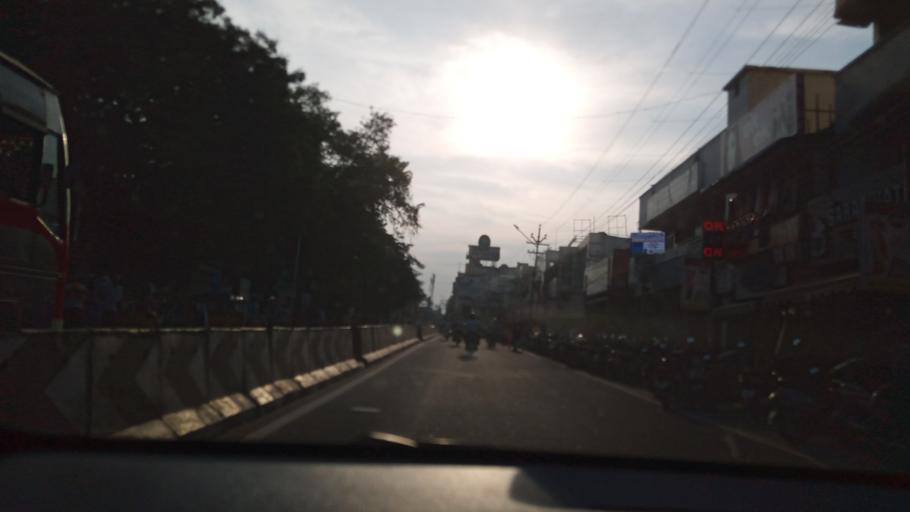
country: IN
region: Tamil Nadu
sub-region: Coimbatore
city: Coimbatore
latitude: 10.9938
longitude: 76.9621
